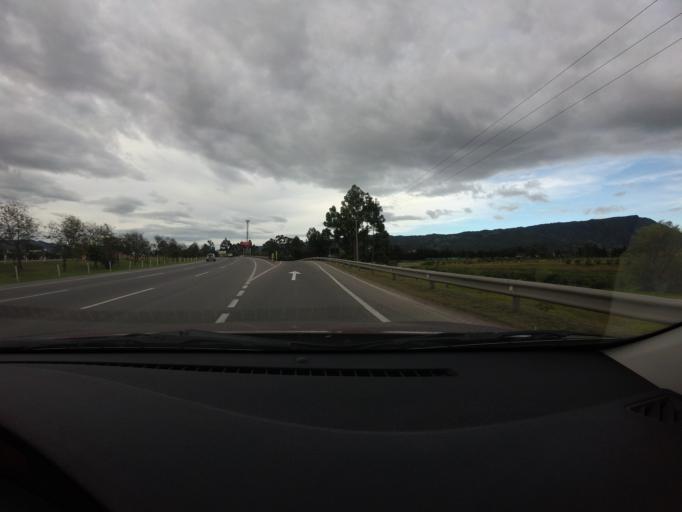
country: CO
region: Cundinamarca
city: Sopo
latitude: 4.9391
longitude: -73.9613
